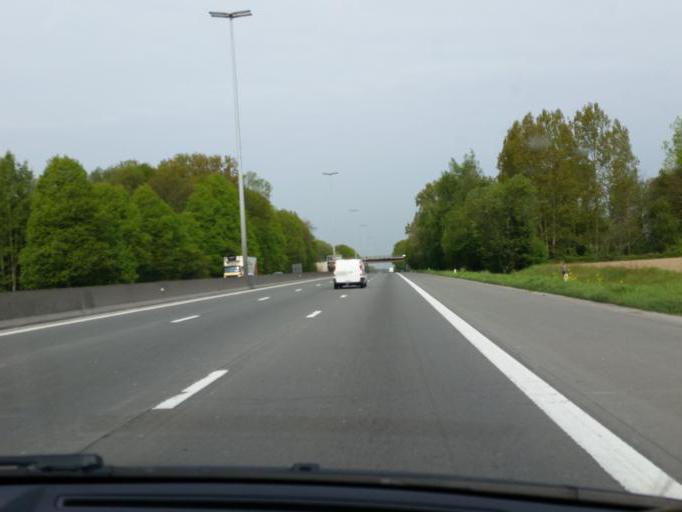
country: BE
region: Flanders
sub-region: Provincie Oost-Vlaanderen
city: Denderleeuw
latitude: 50.8996
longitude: 4.0980
